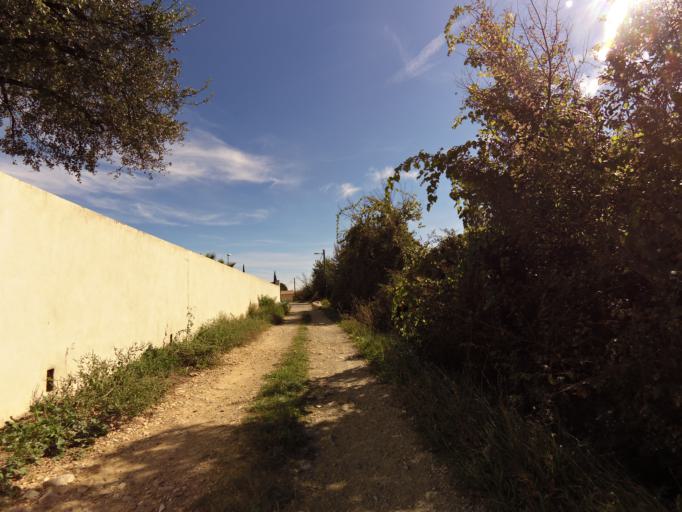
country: FR
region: Languedoc-Roussillon
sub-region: Departement du Gard
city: Vergeze
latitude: 43.7472
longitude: 4.2109
